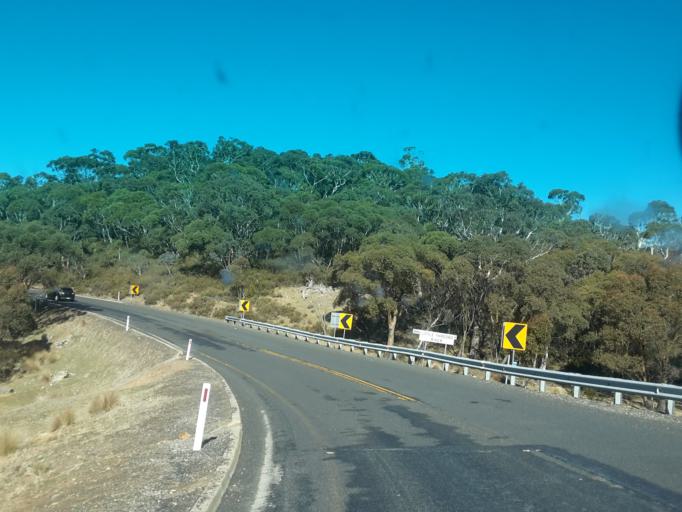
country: AU
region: New South Wales
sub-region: Snowy River
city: Jindabyne
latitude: -36.4507
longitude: 148.4459
